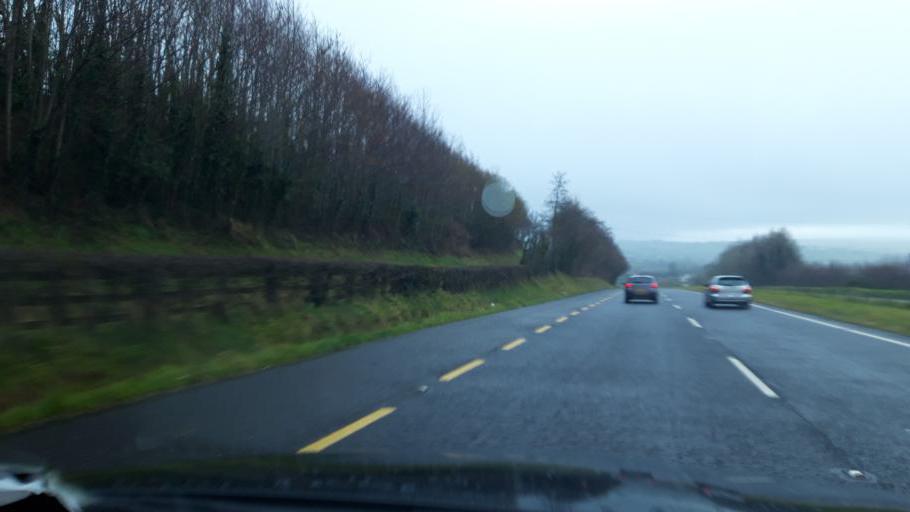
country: IE
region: Ulster
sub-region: County Donegal
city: Letterkenny
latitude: 54.9494
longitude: -7.6527
